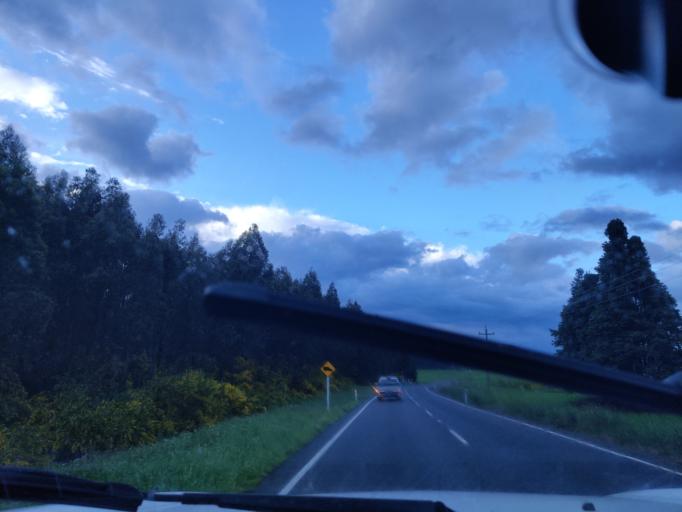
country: NZ
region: Waikato
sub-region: South Waikato District
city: Tokoroa
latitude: -38.3632
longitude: 175.8066
